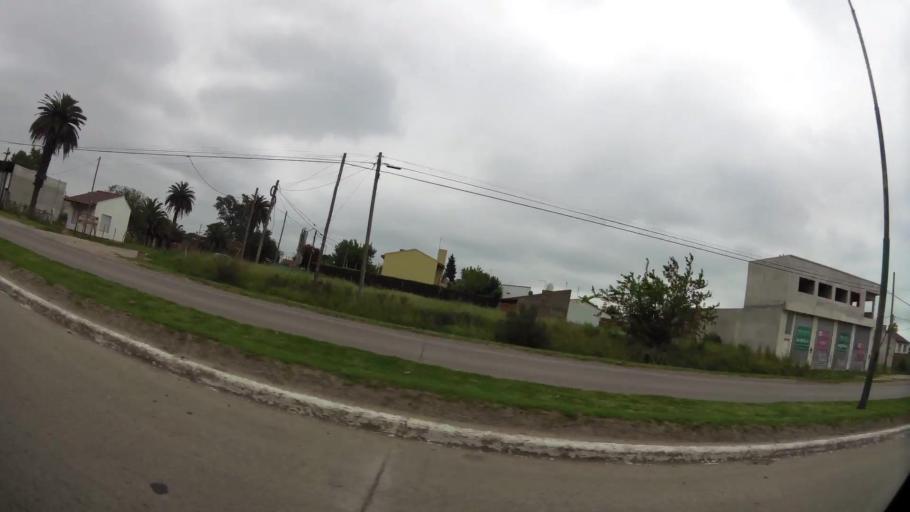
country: AR
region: Buenos Aires
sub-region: Partido de La Plata
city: La Plata
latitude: -35.0100
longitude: -58.0642
